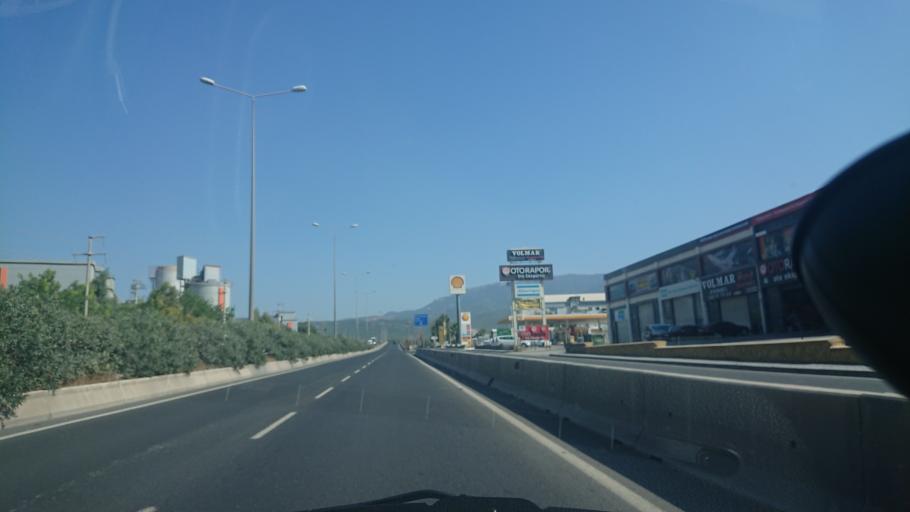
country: TR
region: Izmir
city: Bornova
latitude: 38.4544
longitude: 27.2602
